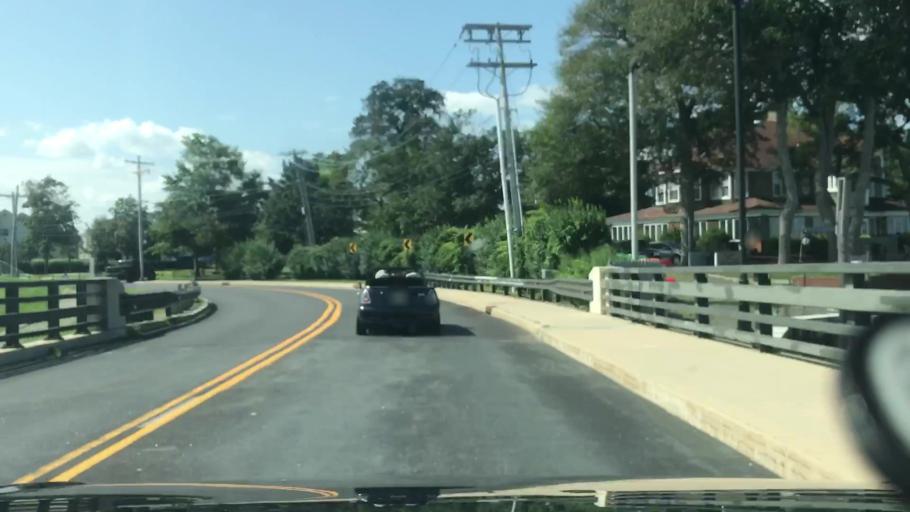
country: US
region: New Jersey
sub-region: Monmouth County
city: Monmouth Beach
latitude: 40.3275
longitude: -73.9925
